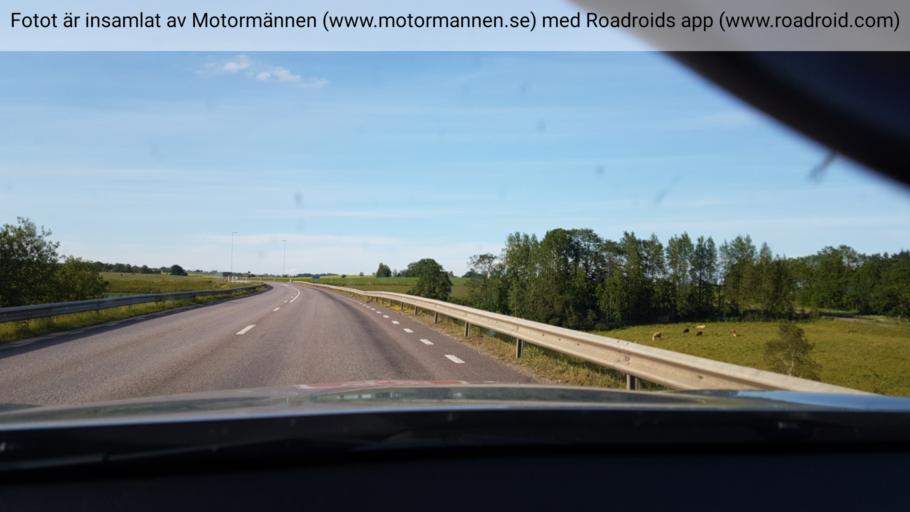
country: SE
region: Vaestra Goetaland
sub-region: Falkopings Kommun
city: Falkoeping
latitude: 58.1322
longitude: 13.5603
